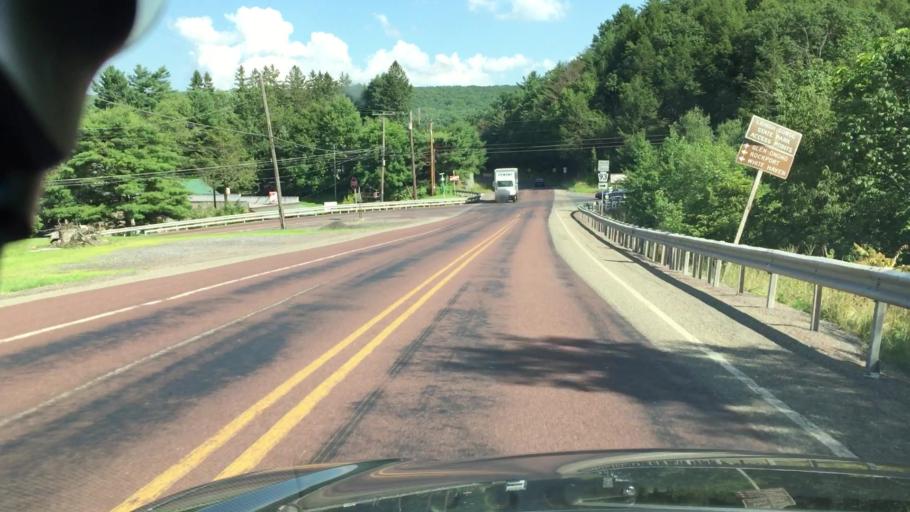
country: US
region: Pennsylvania
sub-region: Carbon County
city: Weatherly
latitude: 40.9194
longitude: -75.8589
